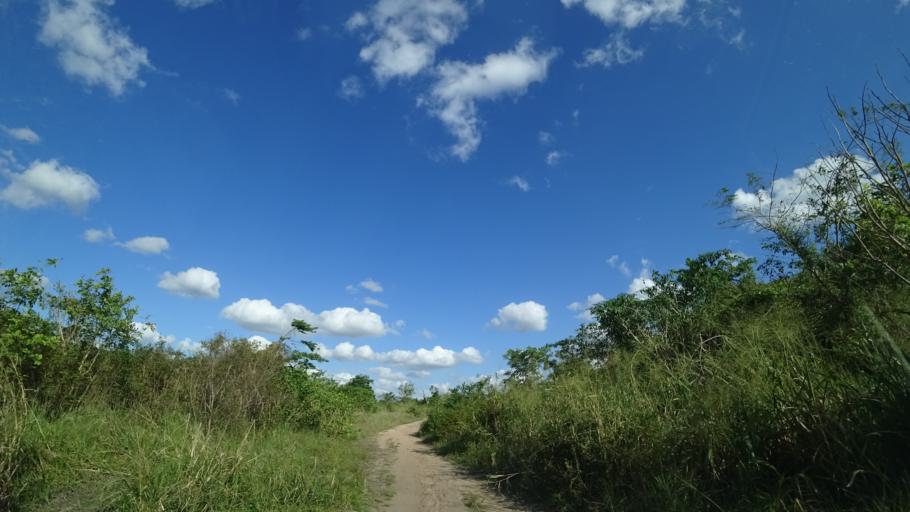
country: MZ
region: Sofala
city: Dondo
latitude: -19.4269
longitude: 34.7240
